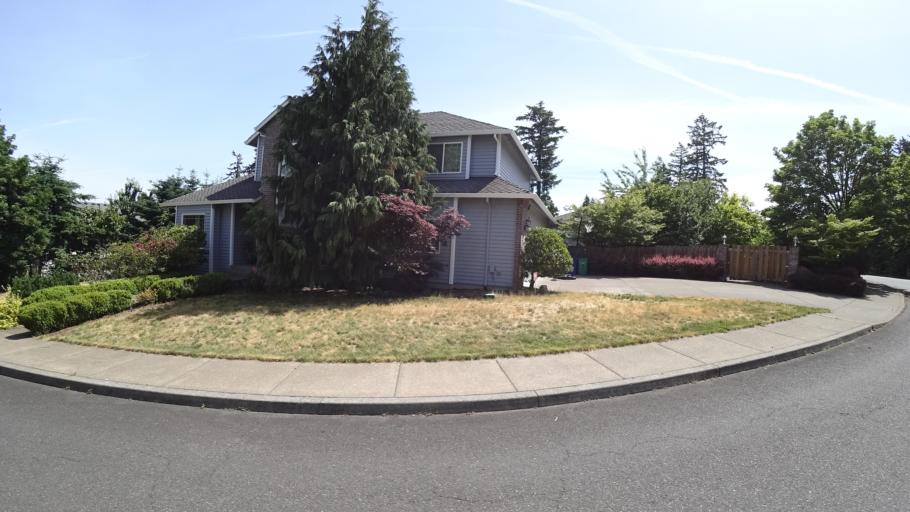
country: US
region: Oregon
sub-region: Multnomah County
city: Fairview
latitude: 45.5431
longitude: -122.5039
